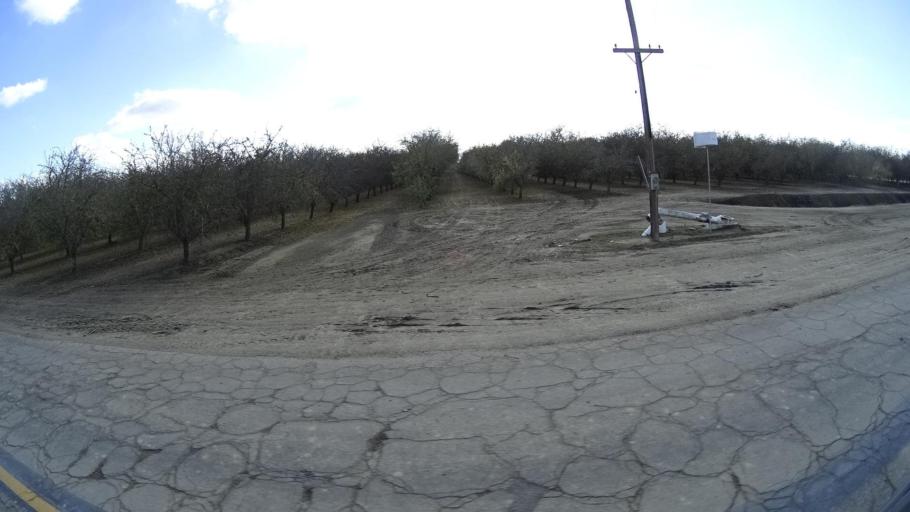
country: US
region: California
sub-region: Kern County
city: Delano
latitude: 35.7322
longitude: -119.3645
